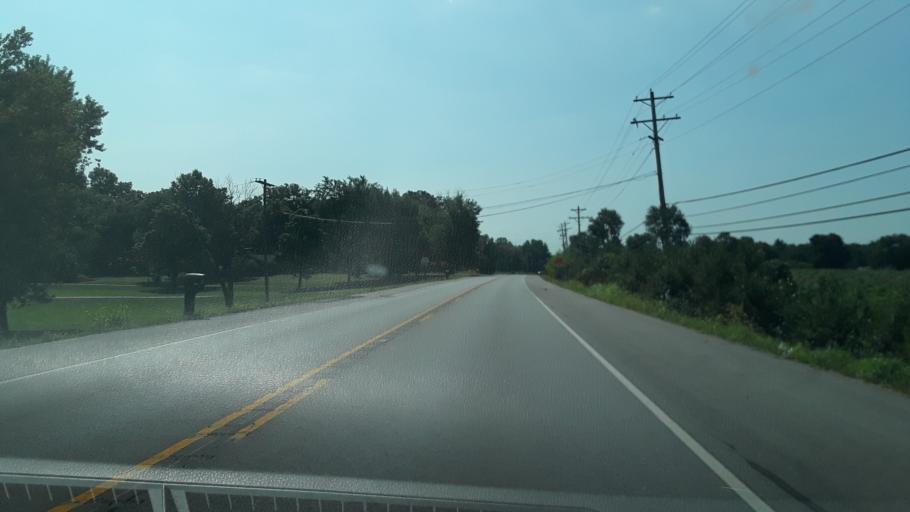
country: US
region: Indiana
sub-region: Clark County
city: Sellersburg
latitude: 38.3927
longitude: -85.7756
